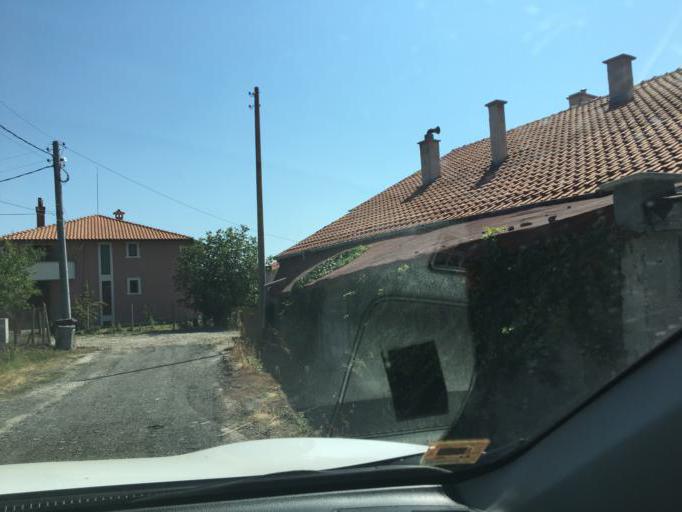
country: BG
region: Burgas
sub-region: Obshtina Kameno
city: Kameno
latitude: 42.6328
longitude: 27.3894
